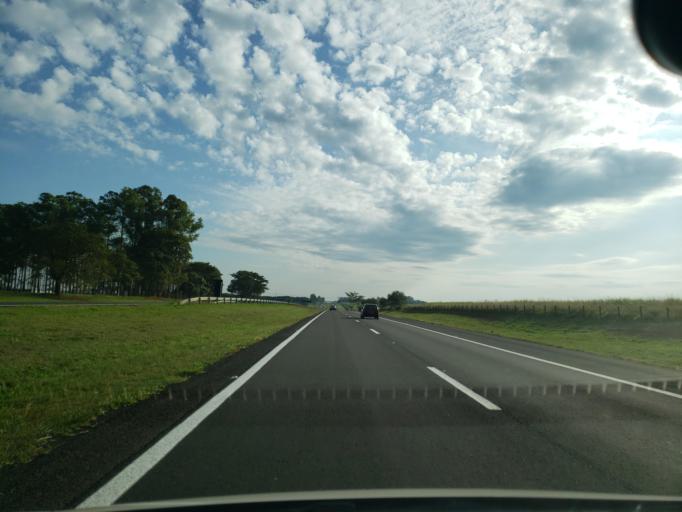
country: BR
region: Sao Paulo
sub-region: Guararapes
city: Guararapes
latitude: -21.2020
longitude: -50.5935
